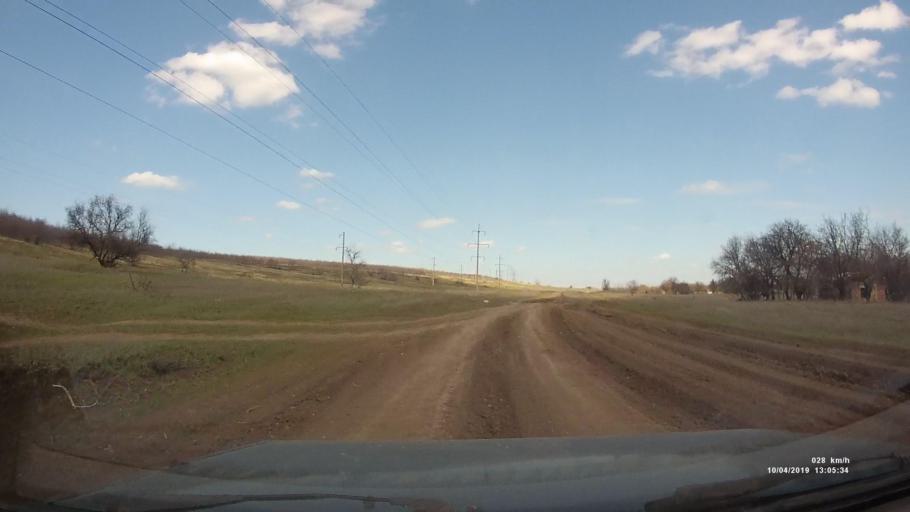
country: RU
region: Rostov
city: Masalovka
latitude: 48.3886
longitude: 40.2331
